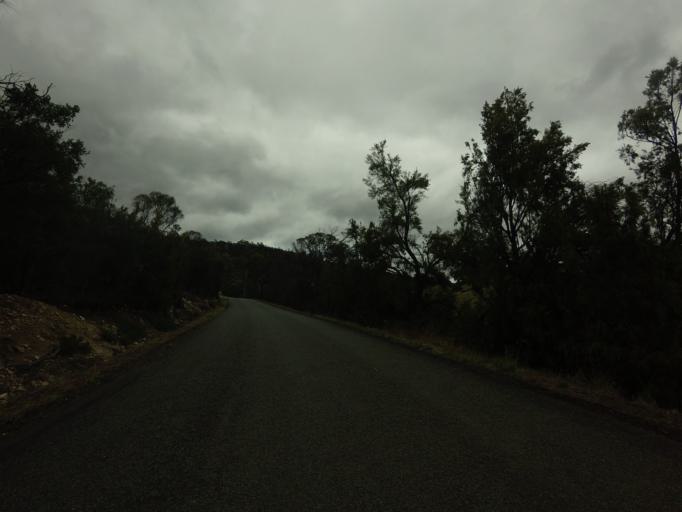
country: AU
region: Tasmania
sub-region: Clarence
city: Cambridge
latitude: -42.7856
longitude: 147.4131
